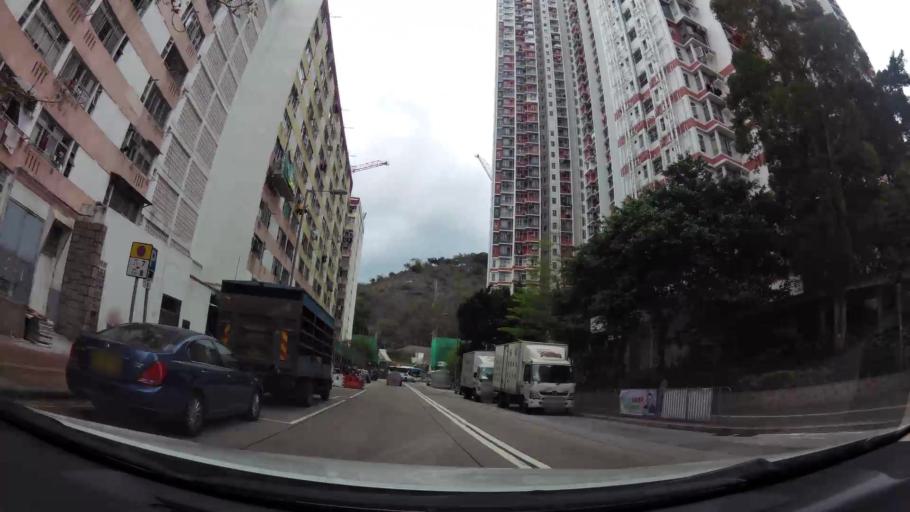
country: HK
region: Sham Shui Po
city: Sham Shui Po
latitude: 22.3337
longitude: 114.1655
